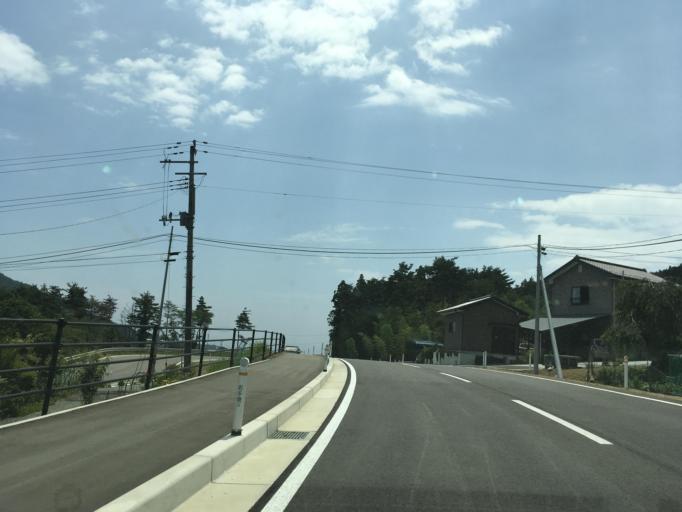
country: JP
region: Iwate
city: Ofunato
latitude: 39.0136
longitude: 141.7103
